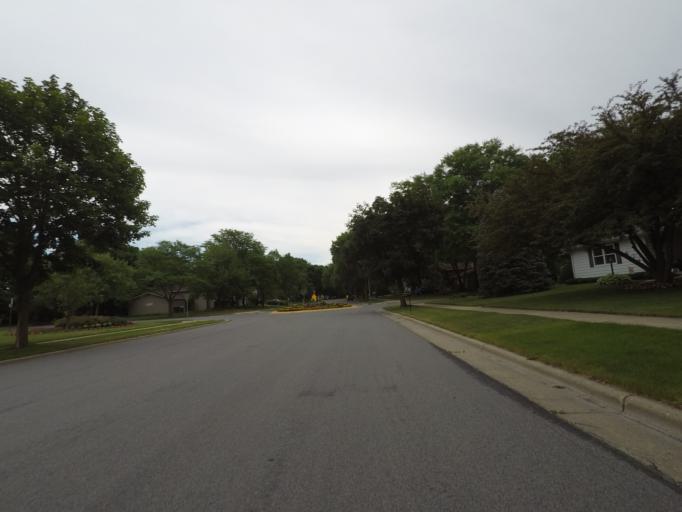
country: US
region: Wisconsin
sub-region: Dane County
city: Middleton
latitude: 43.0802
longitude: -89.5100
